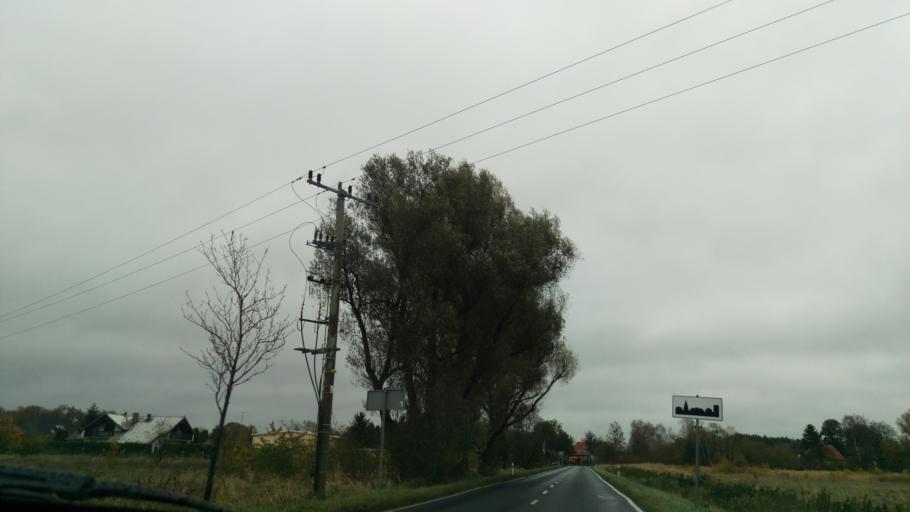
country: PL
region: West Pomeranian Voivodeship
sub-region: Powiat gryfinski
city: Stare Czarnowo
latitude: 53.3945
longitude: 14.7614
